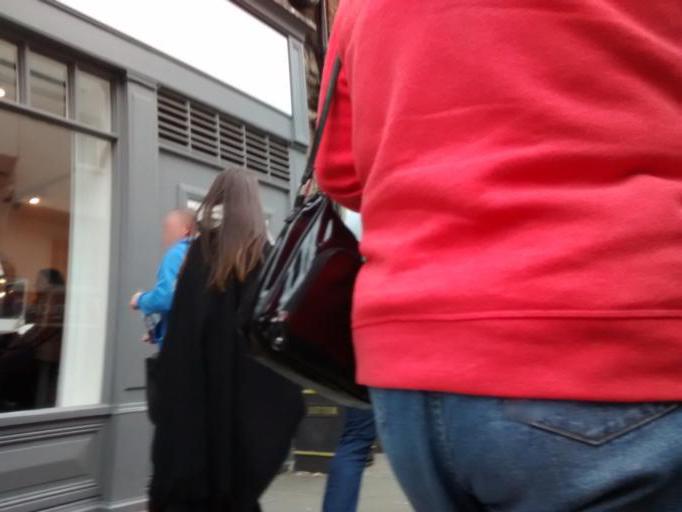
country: GB
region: England
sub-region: City of York
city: York
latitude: 53.9603
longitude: -1.0804
